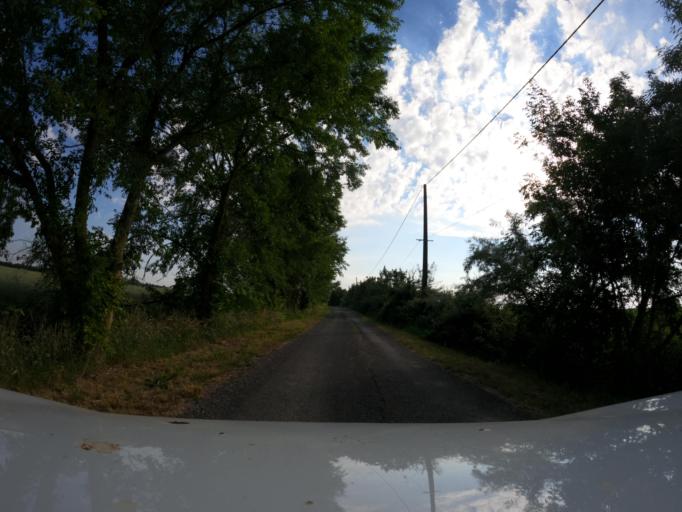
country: FR
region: Pays de la Loire
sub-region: Departement de la Vendee
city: Champagne-les-Marais
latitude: 46.3622
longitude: -1.0847
